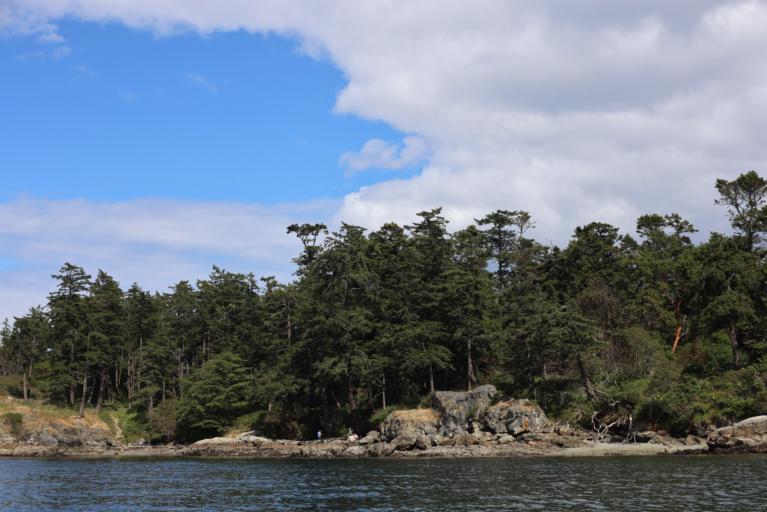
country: CA
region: British Columbia
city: Victoria
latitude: 48.4225
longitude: -123.4211
